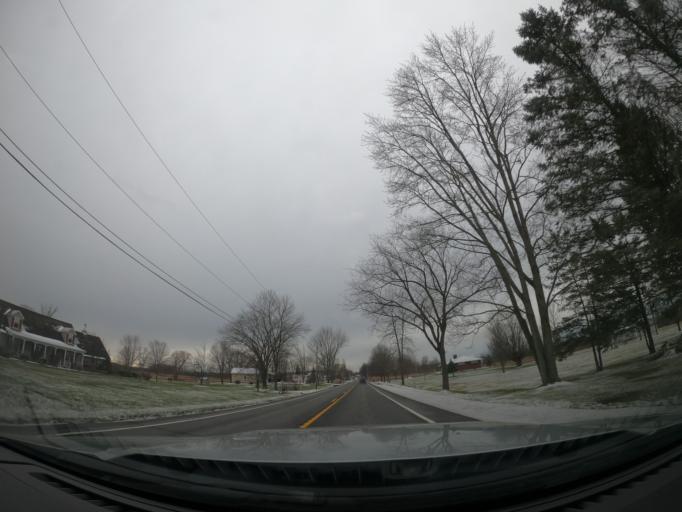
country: US
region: New York
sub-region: Onondaga County
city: Minoa
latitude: 43.1144
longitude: -76.0117
